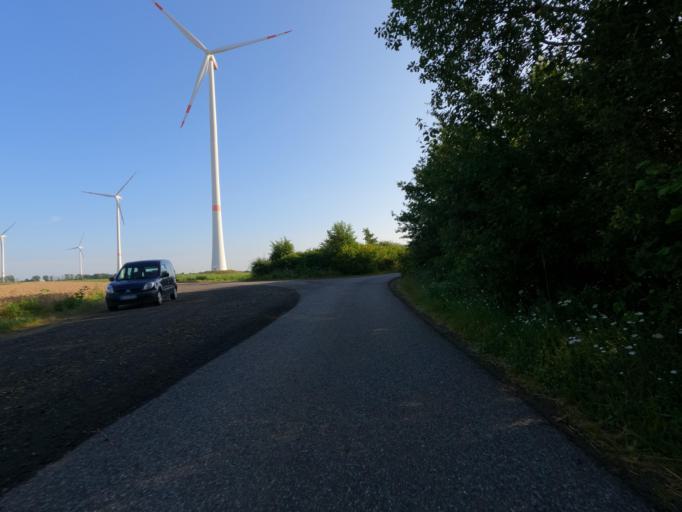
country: DE
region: North Rhine-Westphalia
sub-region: Regierungsbezirk Koln
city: Bedburg
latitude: 51.0449
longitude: 6.5402
